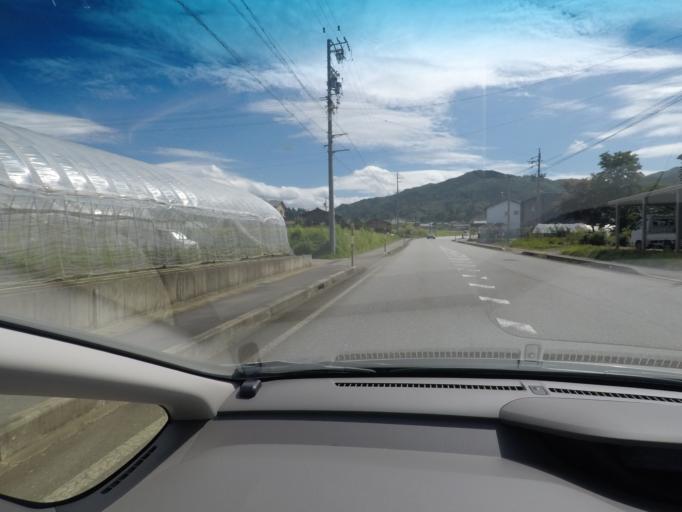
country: JP
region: Gifu
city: Takayama
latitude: 36.1359
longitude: 137.2913
